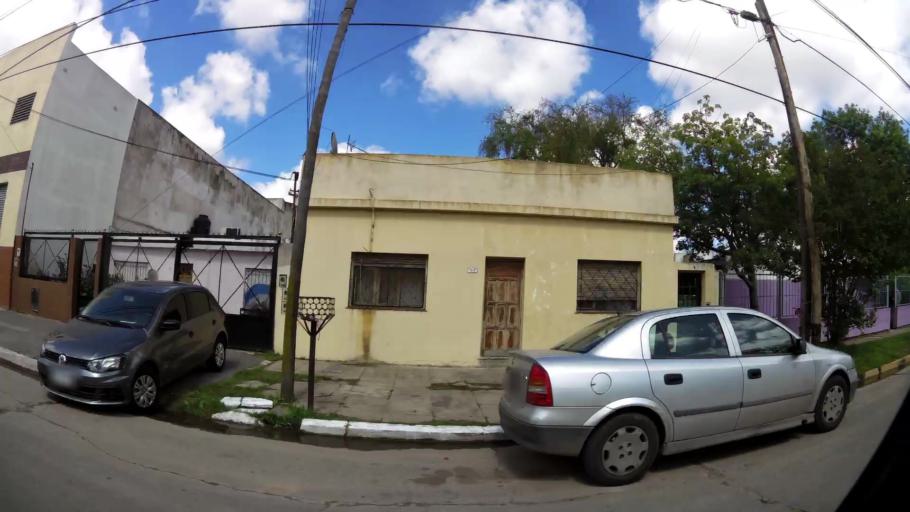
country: AR
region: Buenos Aires
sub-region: Partido de Lanus
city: Lanus
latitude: -34.6884
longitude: -58.4235
